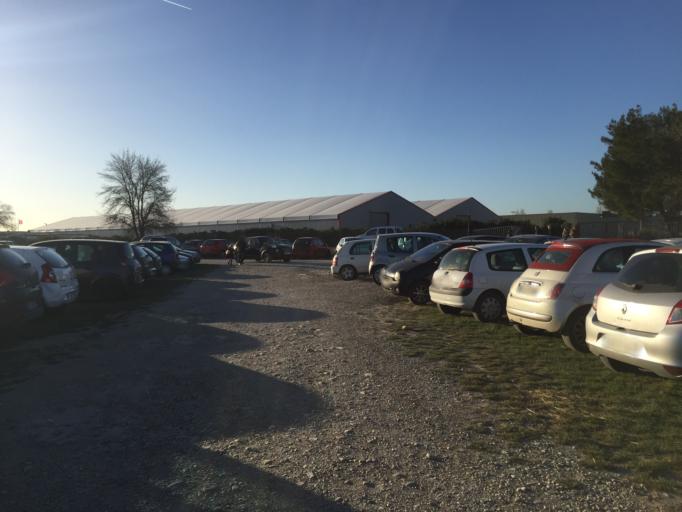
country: FR
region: Provence-Alpes-Cote d'Azur
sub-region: Departement du Vaucluse
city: Montfavet
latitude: 43.9098
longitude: 4.8940
